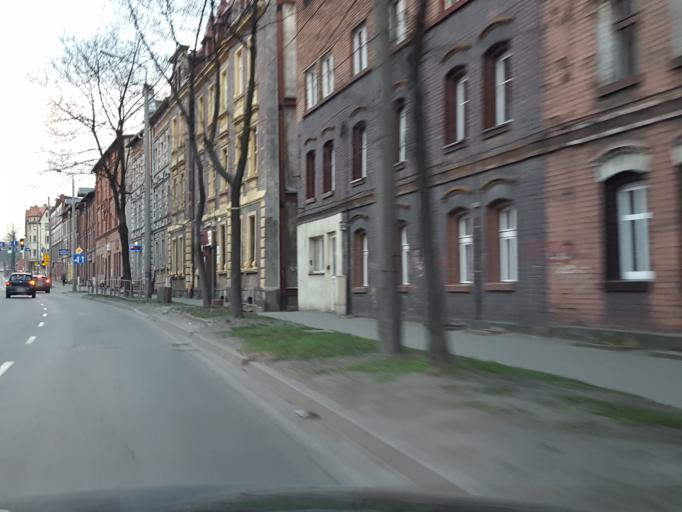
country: PL
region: Silesian Voivodeship
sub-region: Ruda Slaska
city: Ruda Slaska
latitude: 50.2649
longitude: 18.8617
